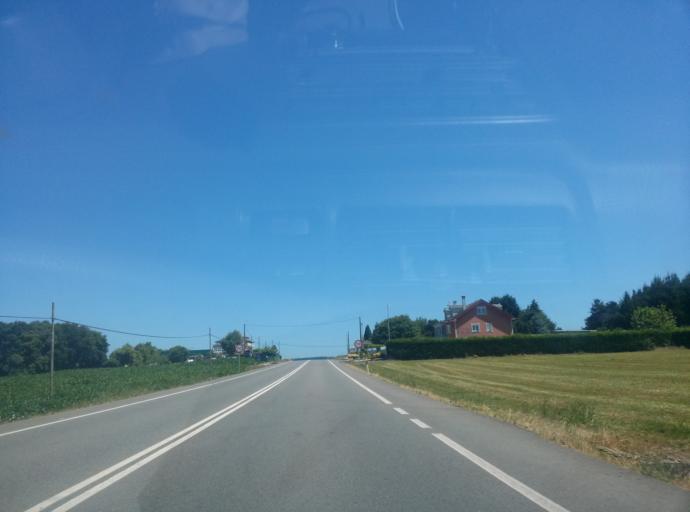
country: ES
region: Galicia
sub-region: Provincia de Lugo
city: Castro de Rei
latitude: 43.2362
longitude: -7.4018
